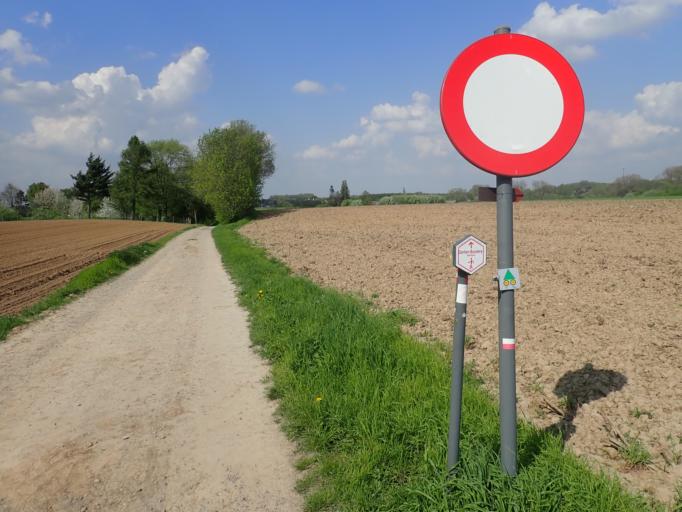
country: BE
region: Flanders
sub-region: Provincie Vlaams-Brabant
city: Wemmel
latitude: 50.9144
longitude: 4.2606
